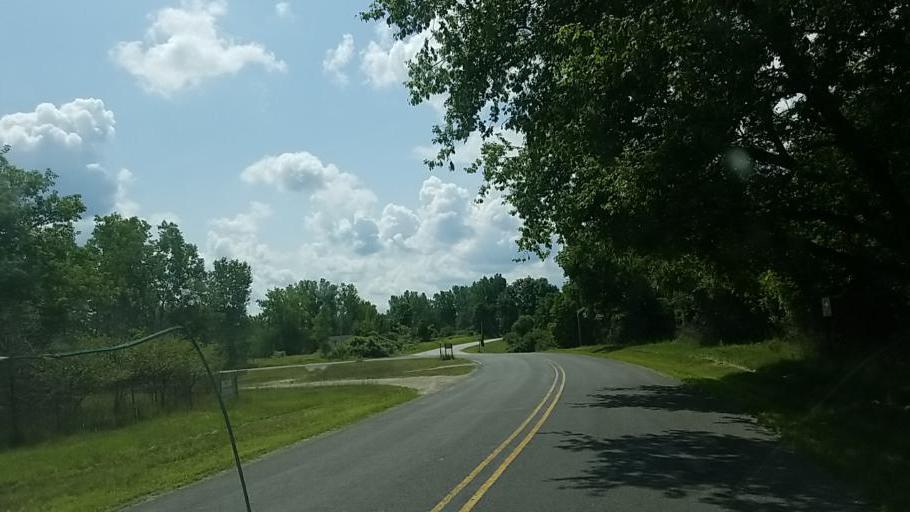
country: US
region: Michigan
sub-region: Muskegon County
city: Ravenna
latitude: 43.2070
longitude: -85.8800
